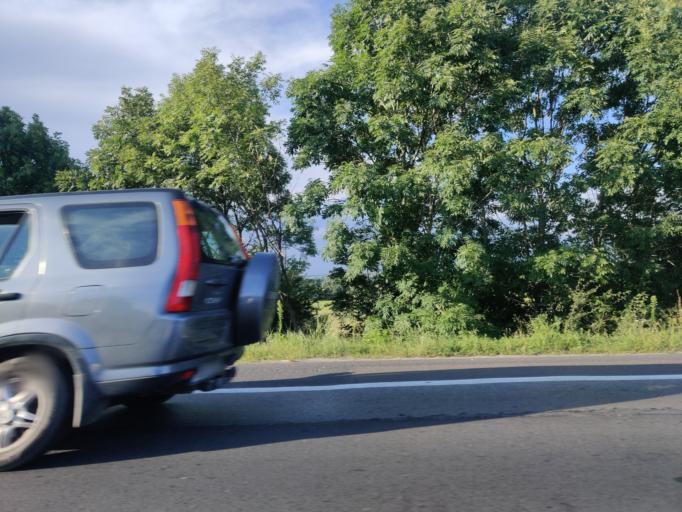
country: PL
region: Greater Poland Voivodeship
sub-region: Konin
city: Konin
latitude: 52.2005
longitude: 18.2846
